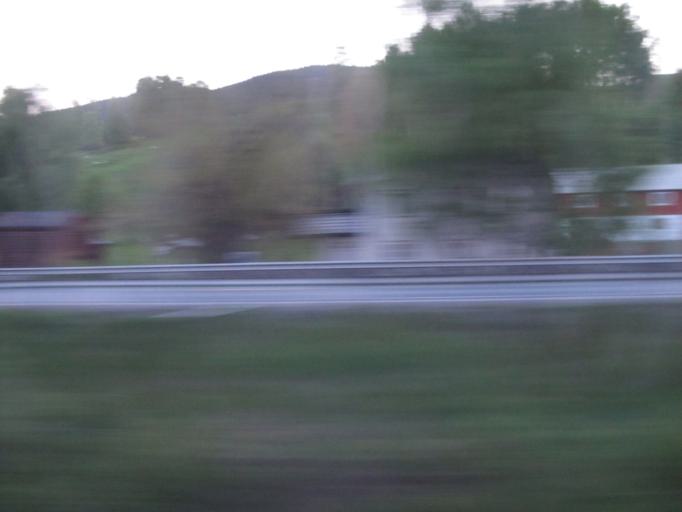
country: NO
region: Oppland
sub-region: Ringebu
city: Ringebu
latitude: 61.5455
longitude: 10.0775
